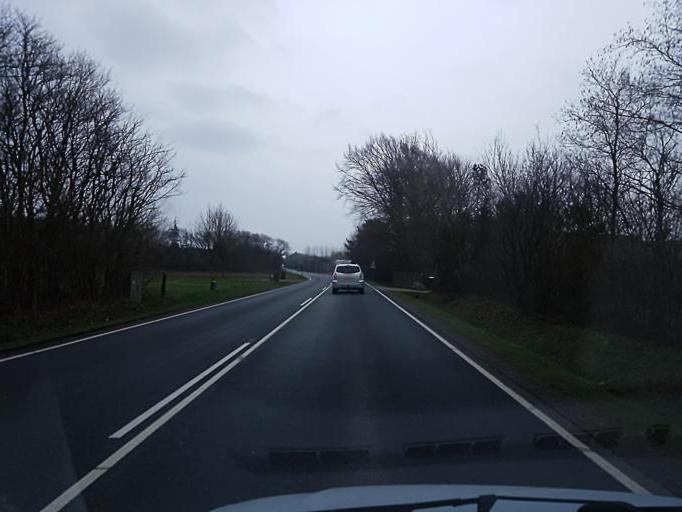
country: DK
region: South Denmark
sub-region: Varde Kommune
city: Varde
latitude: 55.5966
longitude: 8.5062
